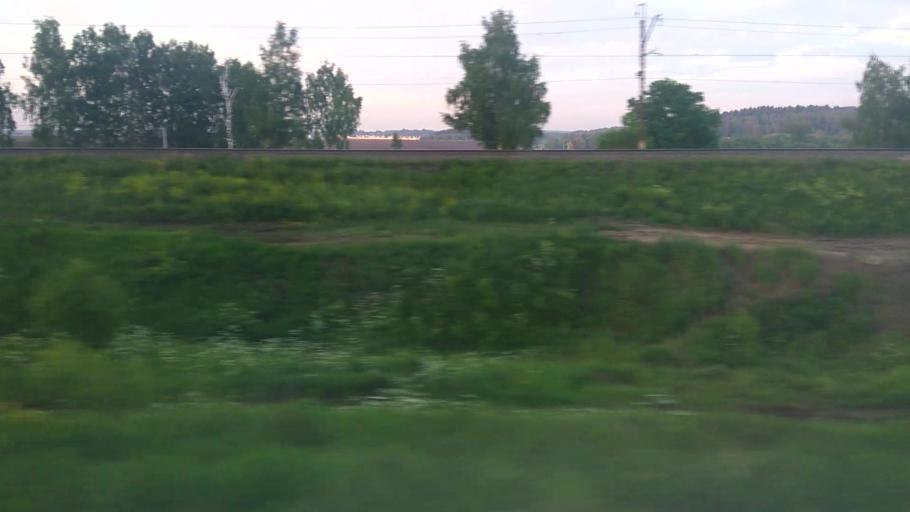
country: RU
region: Moskovskaya
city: Barybino
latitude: 55.2891
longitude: 37.8866
